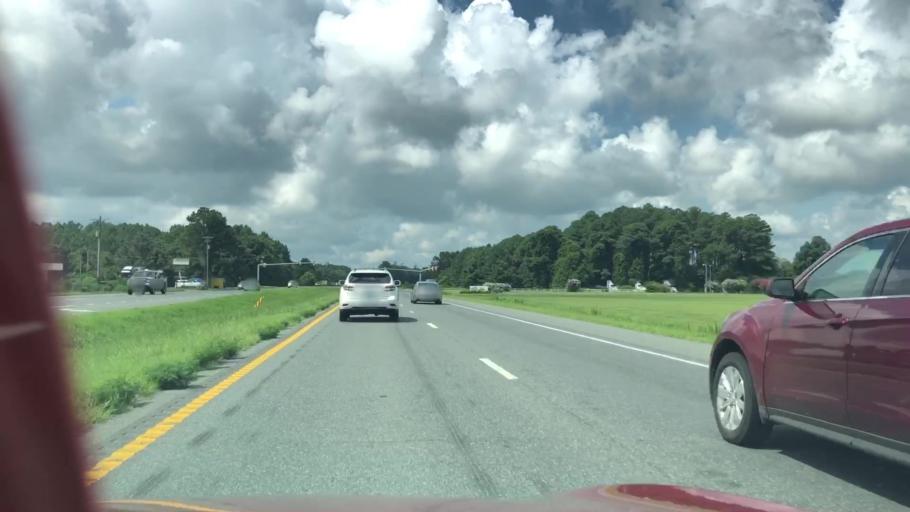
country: US
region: Virginia
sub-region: Accomack County
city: Accomac
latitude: 37.7324
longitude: -75.6554
